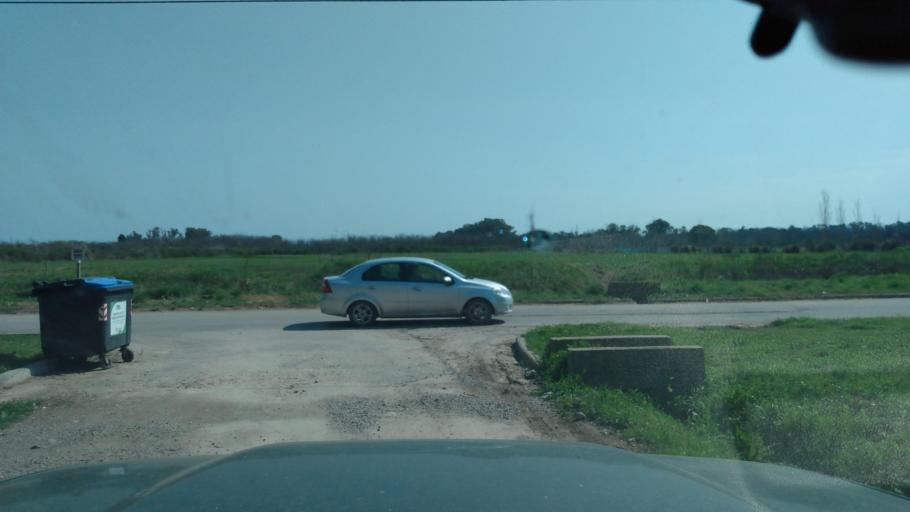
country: AR
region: Buenos Aires
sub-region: Partido de Lujan
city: Lujan
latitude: -34.5462
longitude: -59.1064
